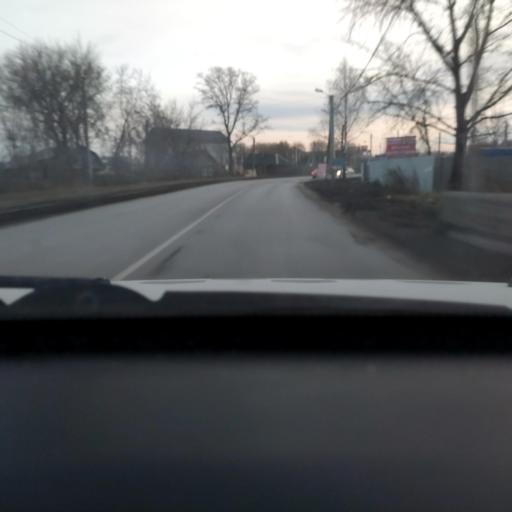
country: RU
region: Perm
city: Kondratovo
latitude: 57.9555
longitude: 56.1350
